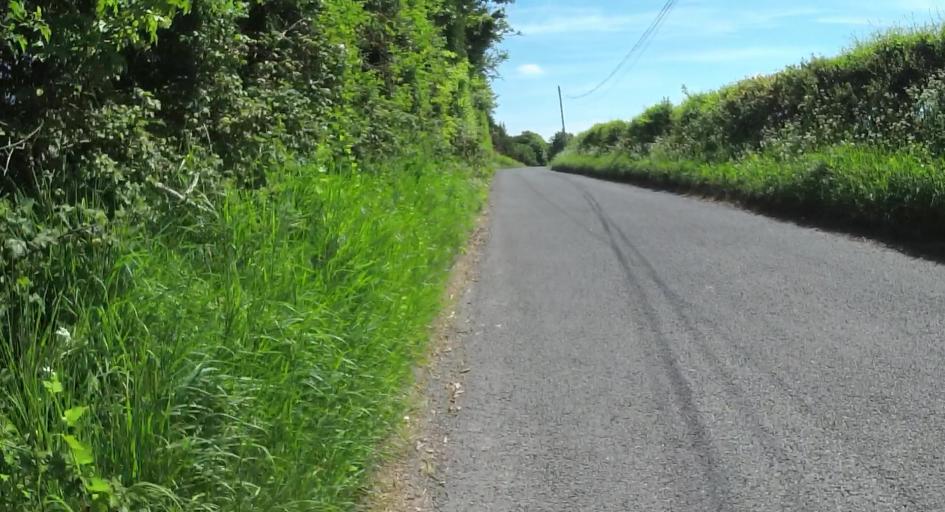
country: GB
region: England
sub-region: Hampshire
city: Four Marks
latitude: 51.1660
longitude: -1.1375
